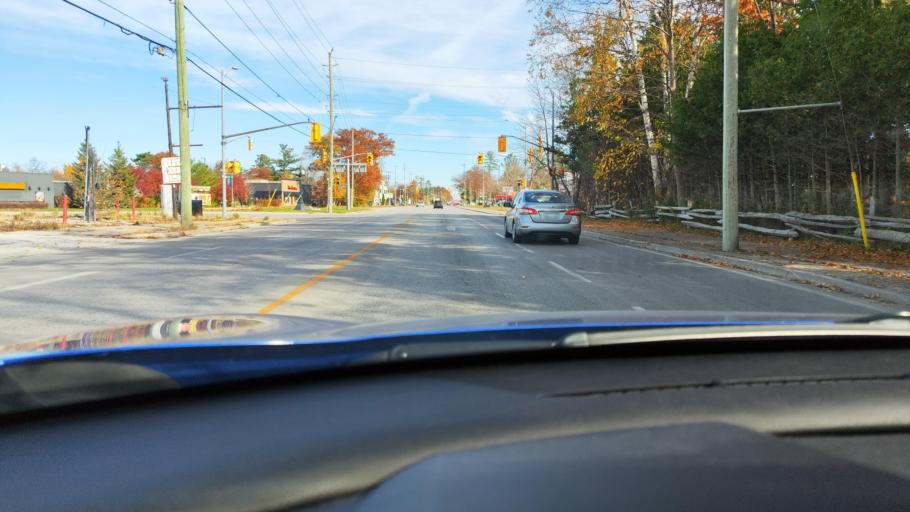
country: CA
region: Ontario
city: Wasaga Beach
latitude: 44.5230
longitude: -80.0047
